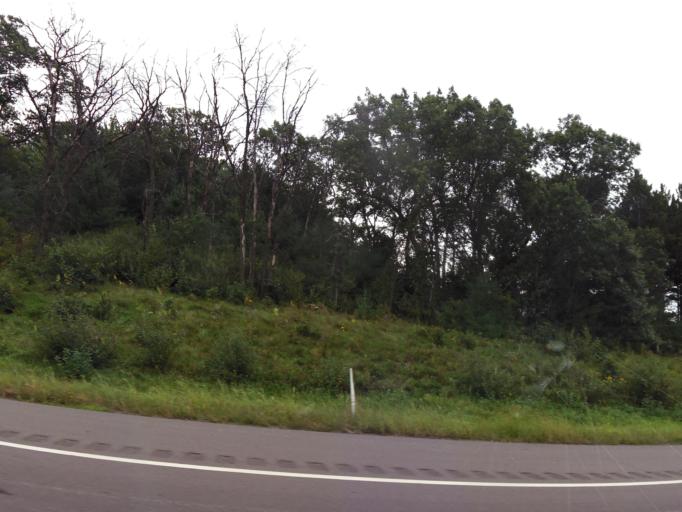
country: US
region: Wisconsin
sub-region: Monroe County
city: Tomah
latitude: 43.9749
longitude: -90.4677
